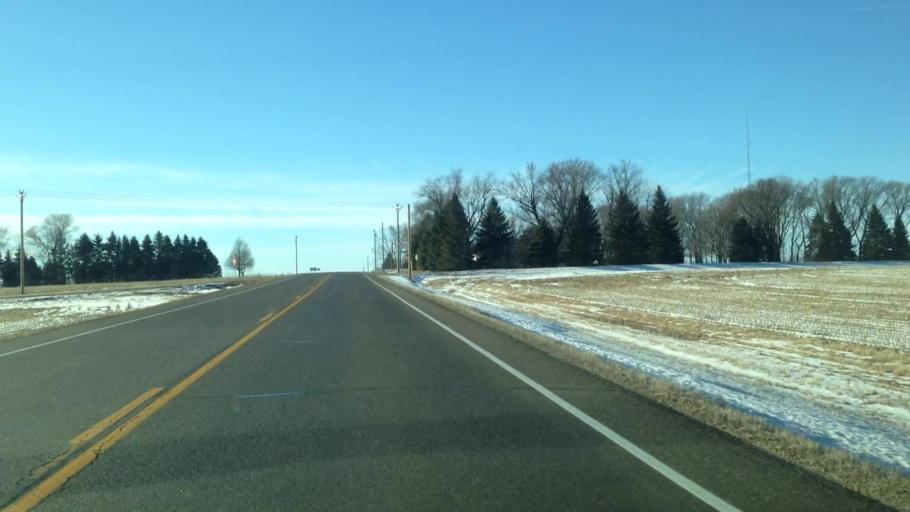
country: US
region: Minnesota
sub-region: Dakota County
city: Farmington
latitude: 44.5879
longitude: -93.0188
